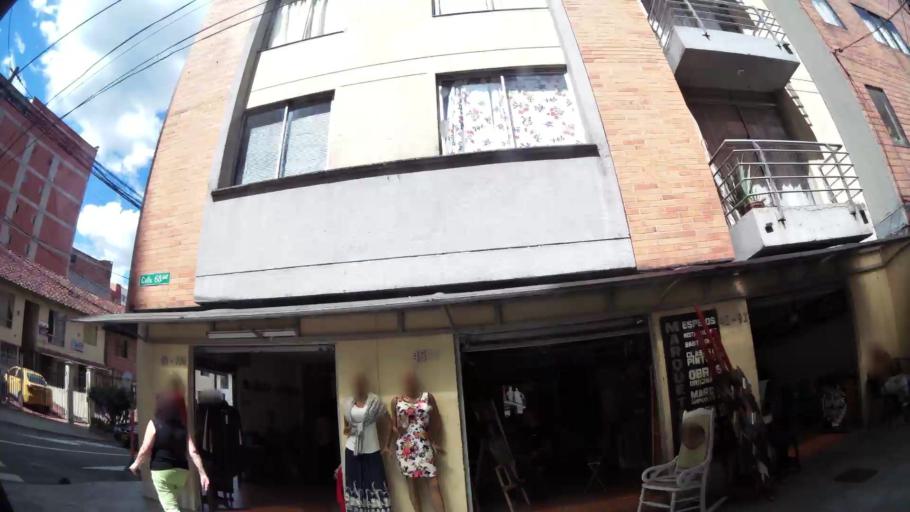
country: CO
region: Antioquia
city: Sabaneta
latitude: 6.1532
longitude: -75.6154
